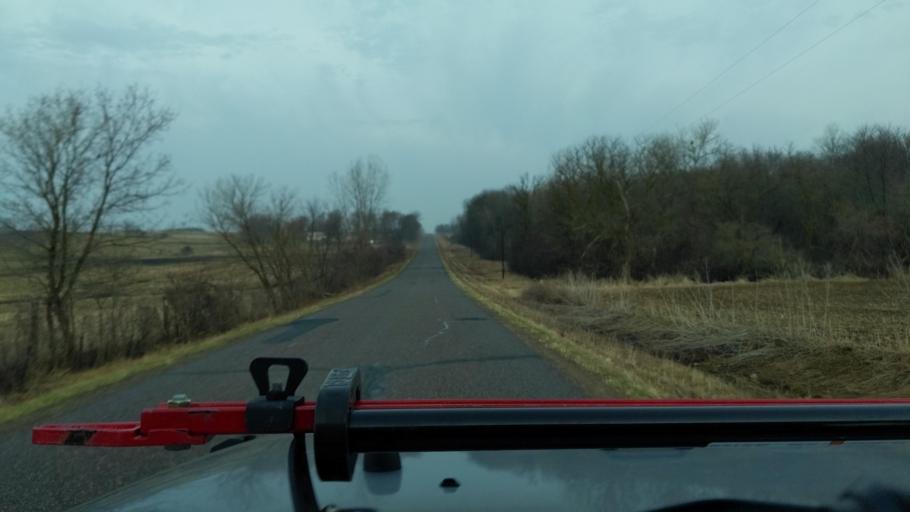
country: US
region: Wisconsin
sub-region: Saint Croix County
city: Hammond
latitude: 44.9344
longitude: -92.4246
